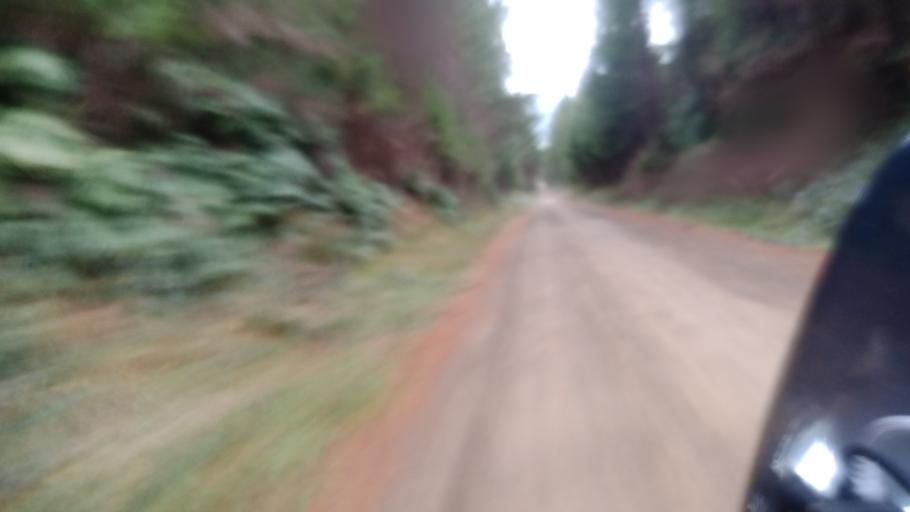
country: NZ
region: Bay of Plenty
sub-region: Whakatane District
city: Murupara
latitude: -38.6331
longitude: 176.7104
